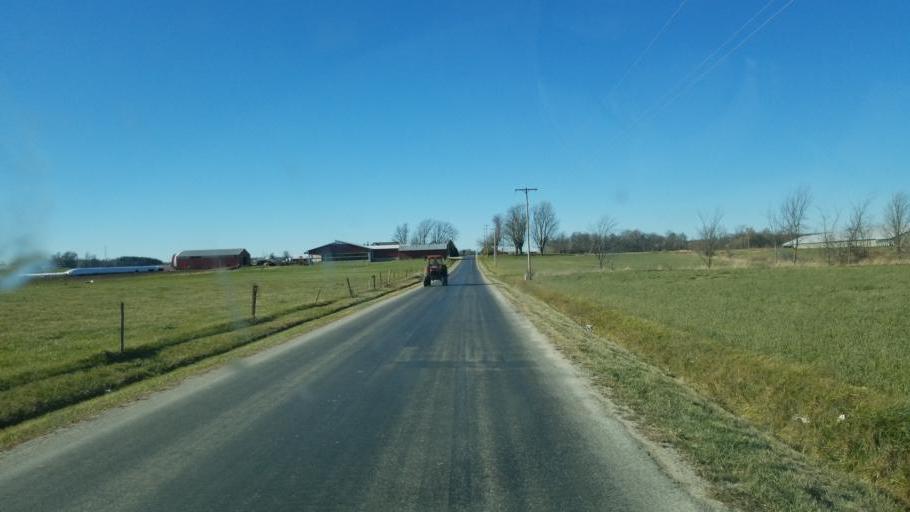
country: US
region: Ohio
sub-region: Huron County
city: Greenwich
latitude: 40.9534
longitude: -82.4464
